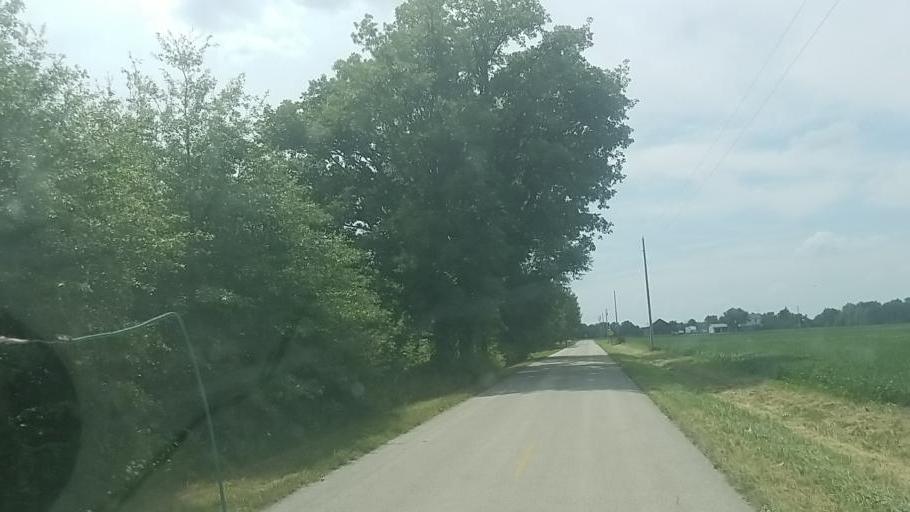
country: US
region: Ohio
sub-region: Hardin County
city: Kenton
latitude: 40.7396
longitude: -83.5975
